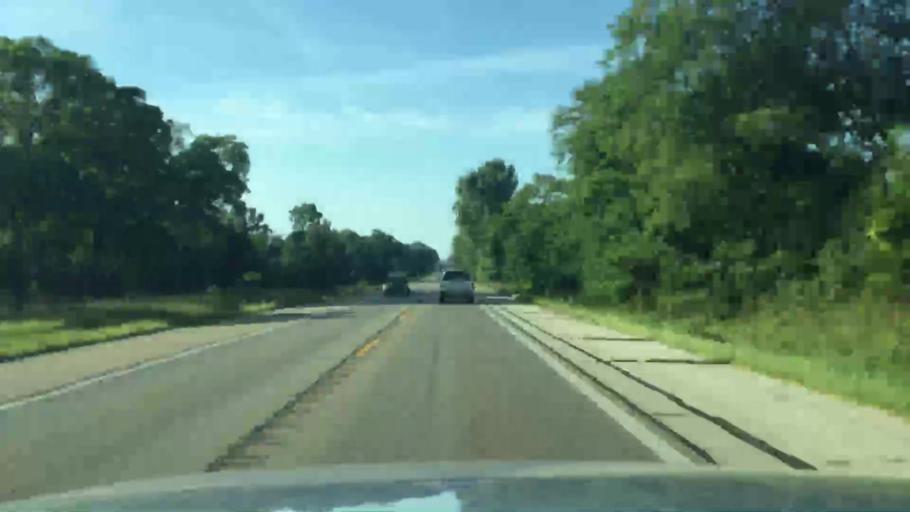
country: US
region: Michigan
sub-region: Jackson County
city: Vandercook Lake
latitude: 42.0984
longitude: -84.3639
